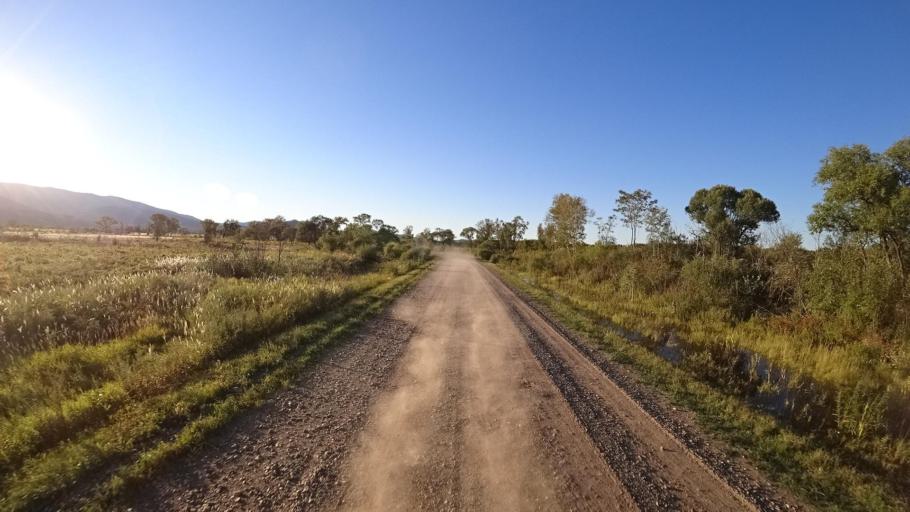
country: RU
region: Primorskiy
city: Kirovskiy
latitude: 44.8136
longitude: 133.6153
